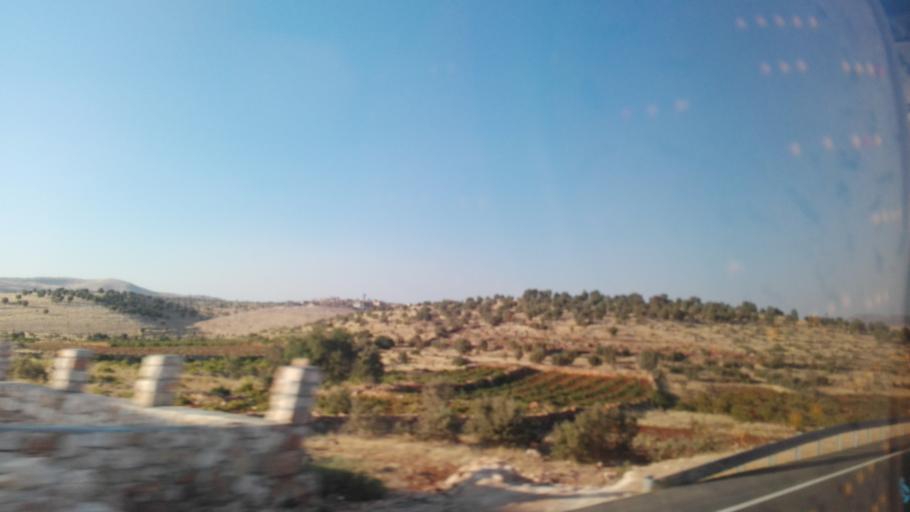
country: TR
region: Mardin
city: Ortaca
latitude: 37.5218
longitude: 41.5883
